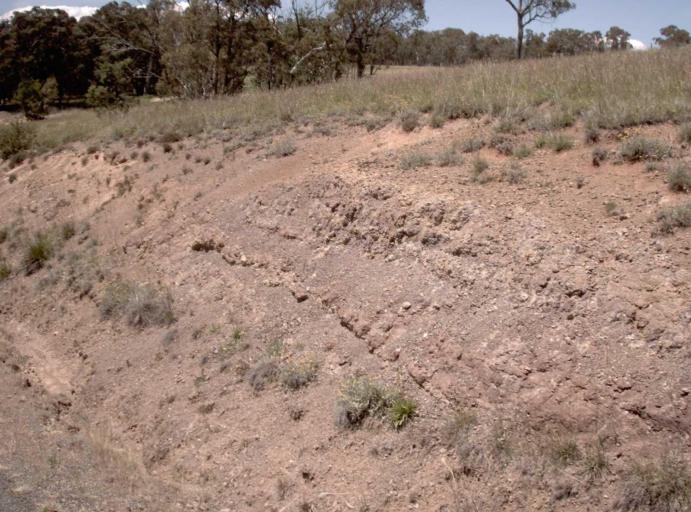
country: AU
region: New South Wales
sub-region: Snowy River
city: Jindabyne
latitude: -37.0794
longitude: 148.2811
